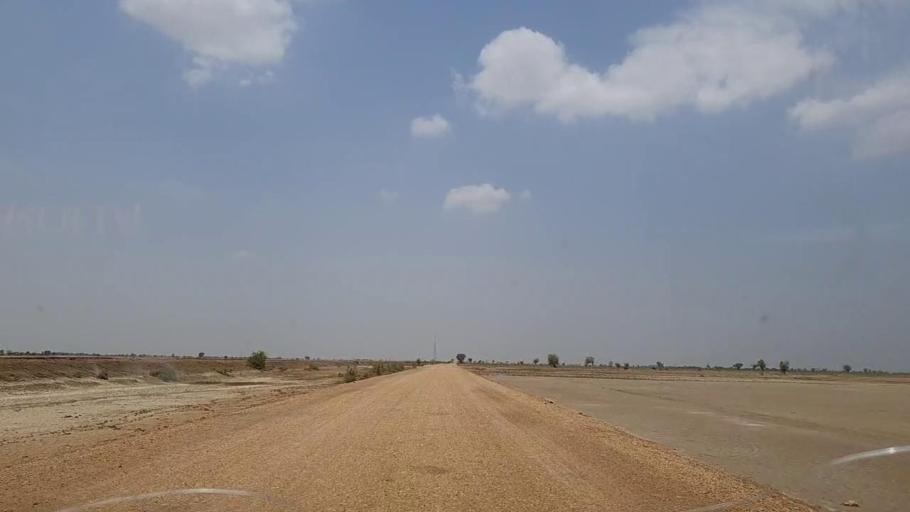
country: PK
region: Sindh
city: Johi
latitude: 26.7724
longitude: 67.6559
